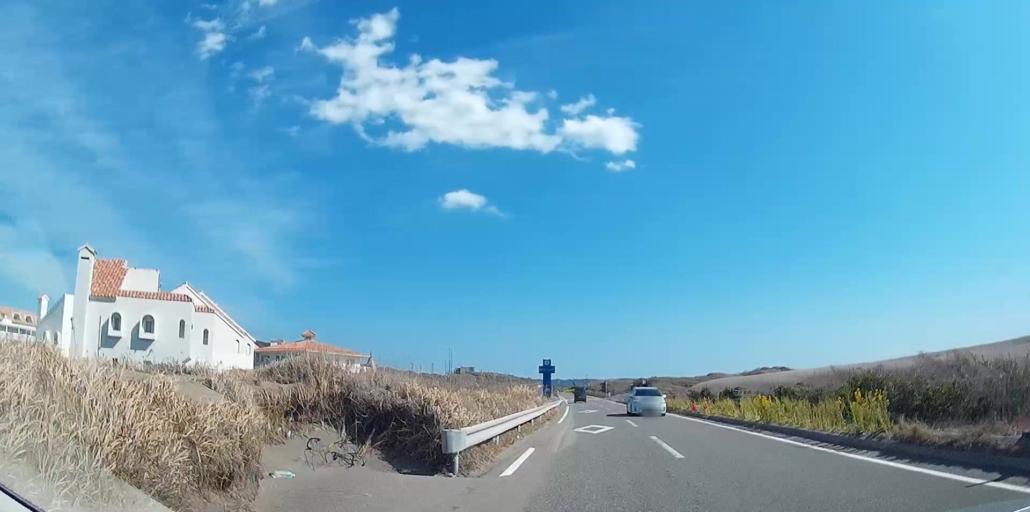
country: JP
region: Chiba
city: Tateyama
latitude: 34.9534
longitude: 139.7902
